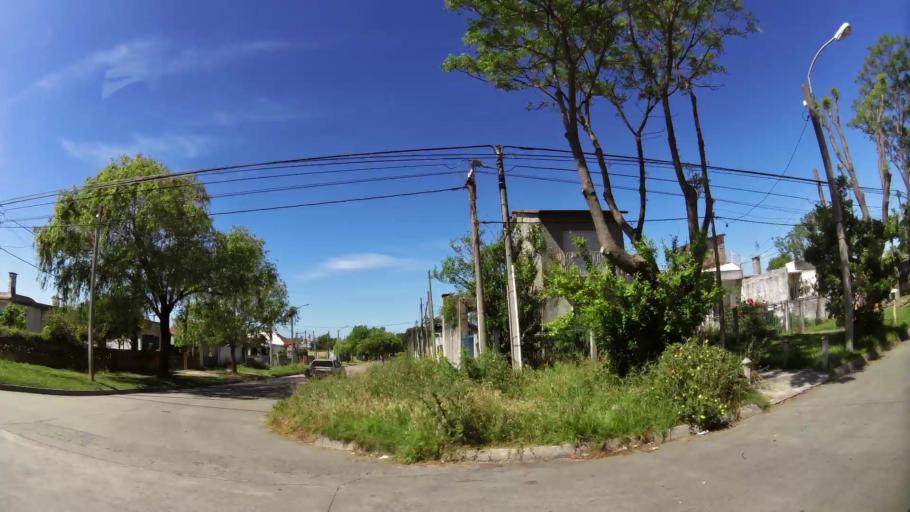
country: UY
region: Canelones
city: Paso de Carrasco
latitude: -34.8548
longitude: -56.1180
